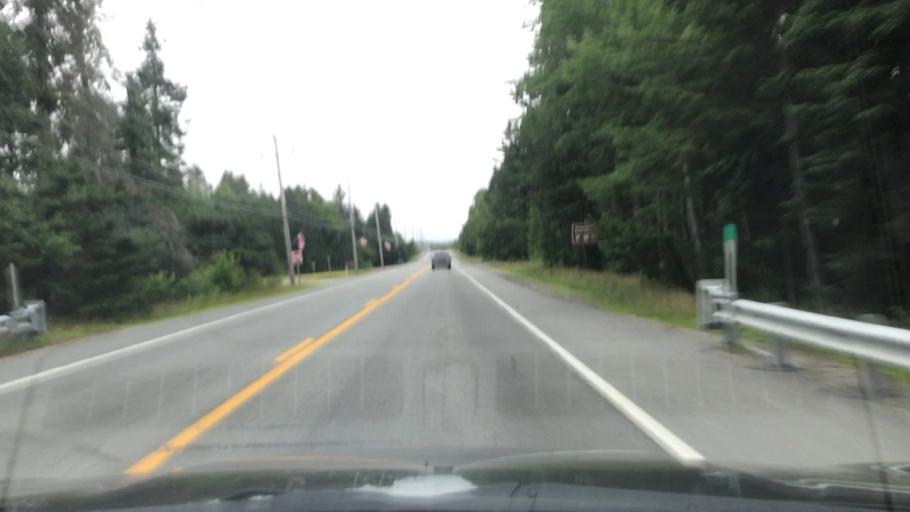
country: US
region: Maine
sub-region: Hancock County
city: Trenton
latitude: 44.4262
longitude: -68.3658
